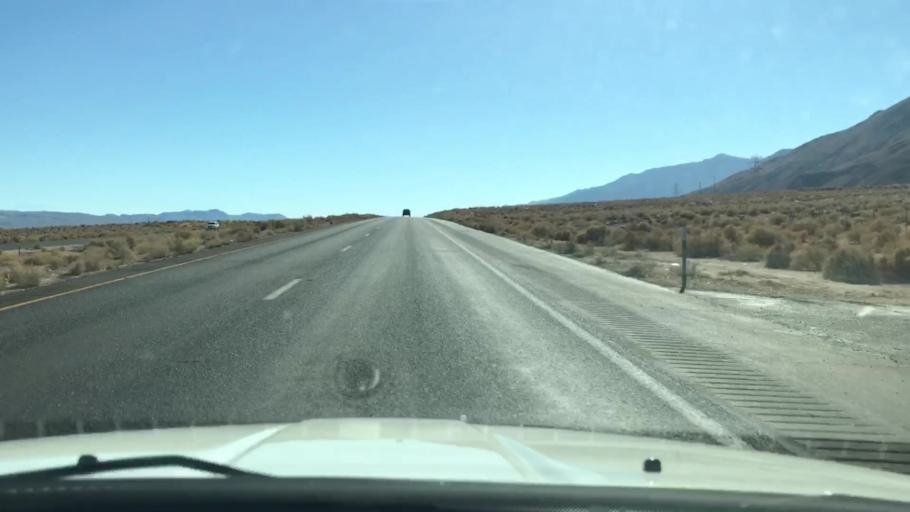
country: US
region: California
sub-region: Inyo County
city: Lone Pine
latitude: 36.3947
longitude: -118.0250
